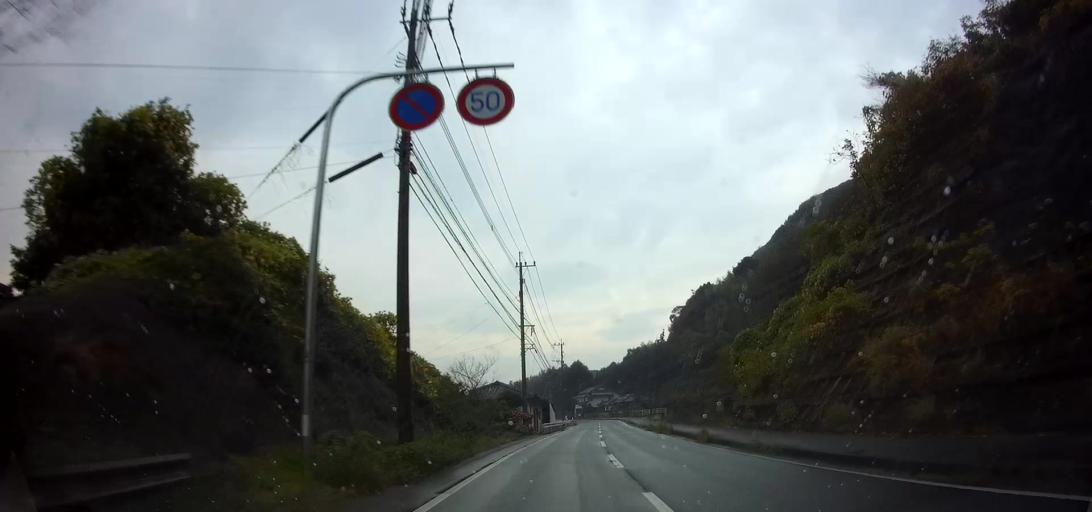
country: JP
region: Nagasaki
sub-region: Isahaya-shi
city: Isahaya
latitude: 32.8481
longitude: 129.9989
